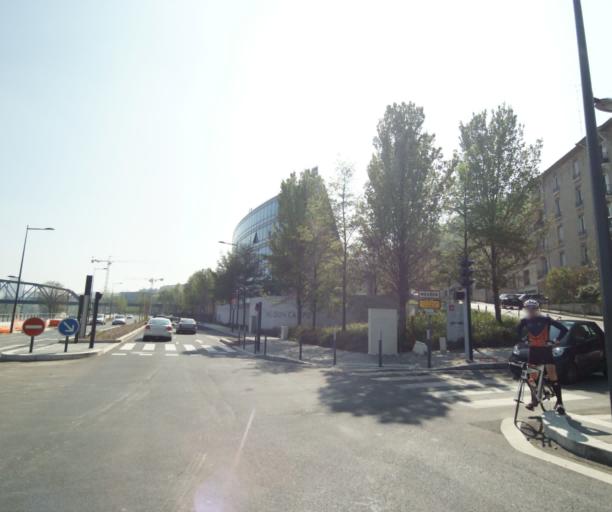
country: FR
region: Ile-de-France
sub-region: Departement des Hauts-de-Seine
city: Meudon
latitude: 48.8222
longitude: 2.2322
